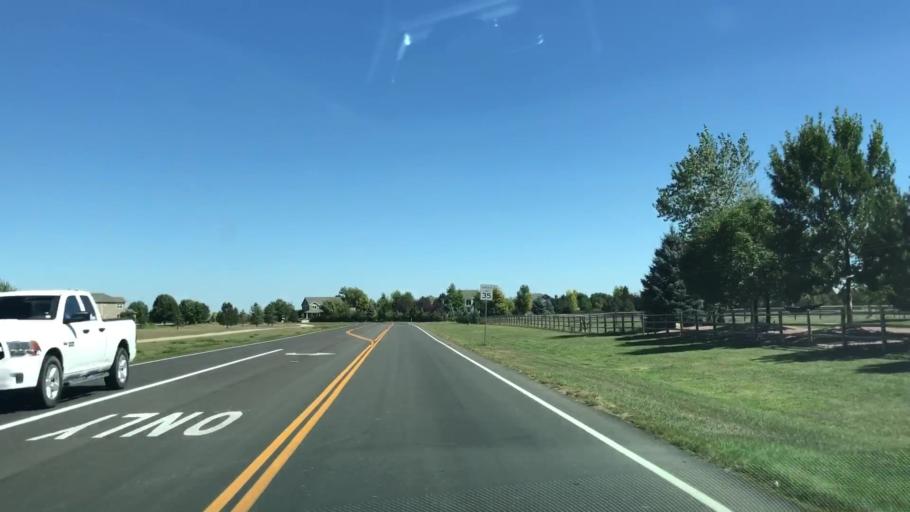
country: US
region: Colorado
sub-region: Weld County
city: Windsor
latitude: 40.4421
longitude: -104.9609
